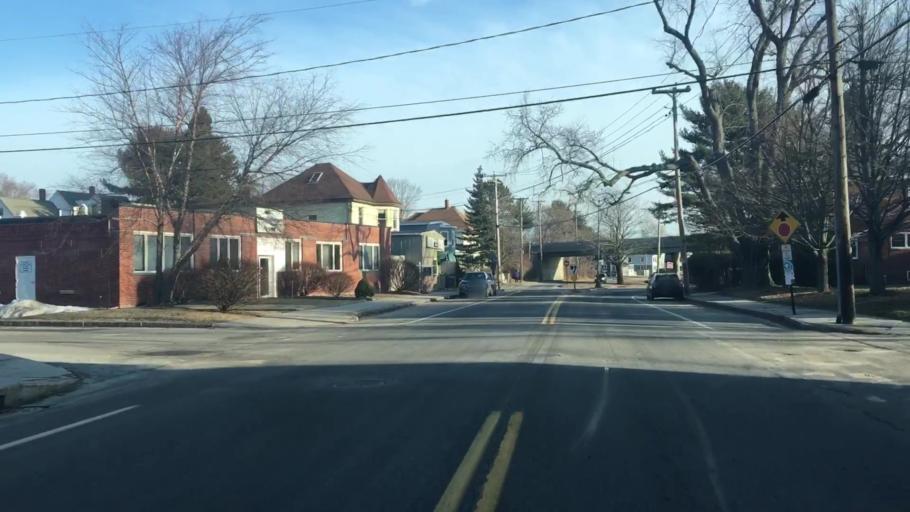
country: US
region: Maine
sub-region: Cumberland County
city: Portland
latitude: 43.6845
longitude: -70.2535
